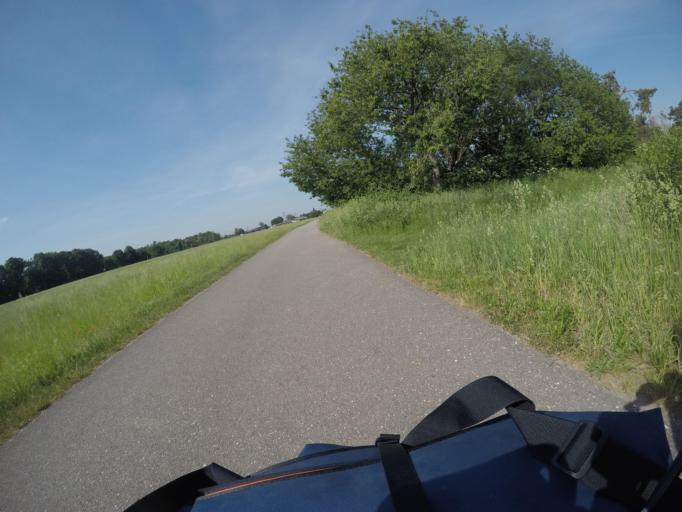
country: DE
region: Baden-Wuerttemberg
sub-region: Karlsruhe Region
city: Bietigheim
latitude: 48.9048
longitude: 8.2792
